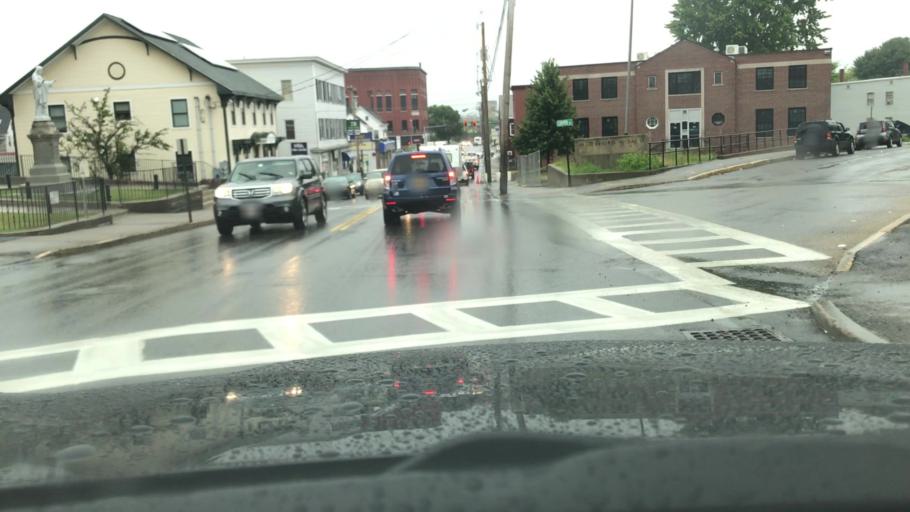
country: US
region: Maine
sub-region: York County
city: Biddeford
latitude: 43.4935
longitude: -70.4608
